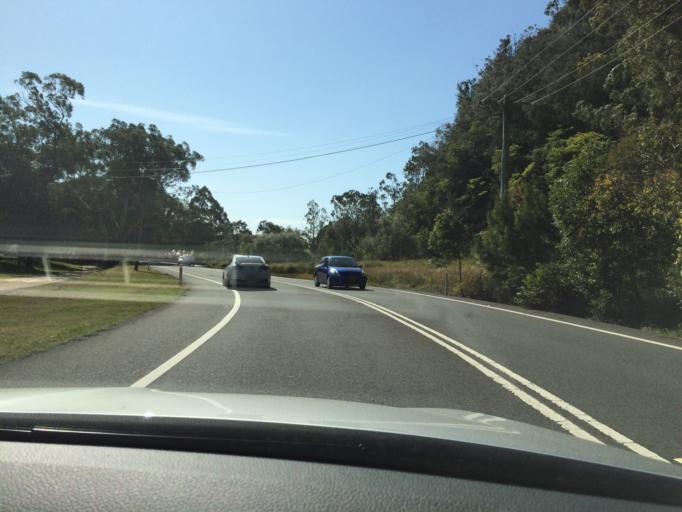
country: AU
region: New South Wales
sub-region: Gosford Shire
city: Ettalong Beach
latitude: -33.5052
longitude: 151.3313
